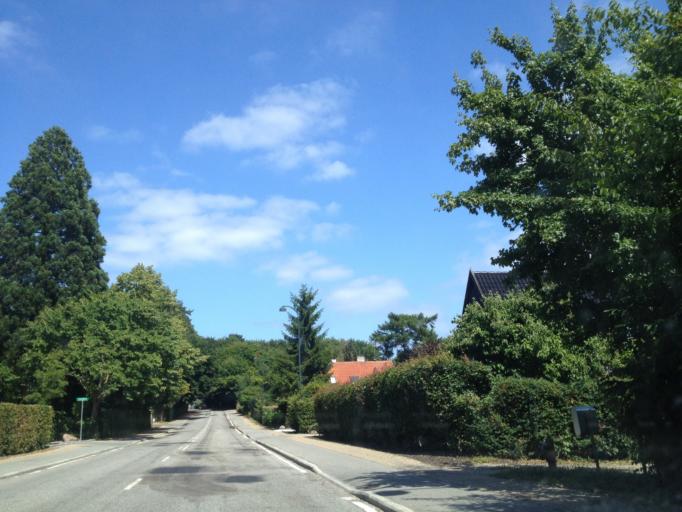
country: DK
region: Capital Region
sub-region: Rudersdal Kommune
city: Trorod
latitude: 55.8408
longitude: 12.5472
